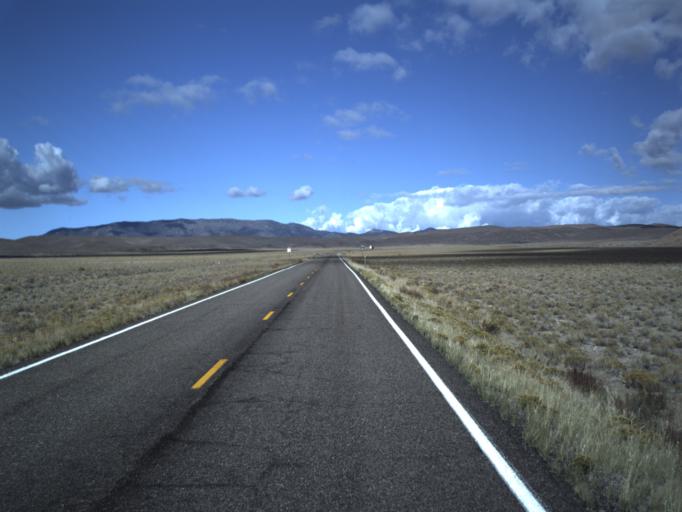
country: US
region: Utah
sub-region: Beaver County
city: Milford
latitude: 38.5727
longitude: -113.7914
